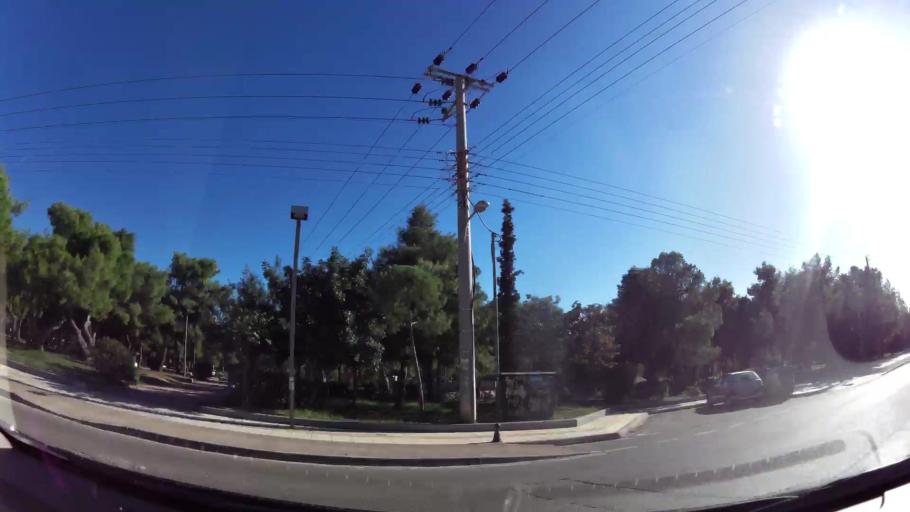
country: GR
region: Attica
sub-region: Nomarchia Anatolikis Attikis
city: Voula
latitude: 37.8444
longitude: 23.7592
